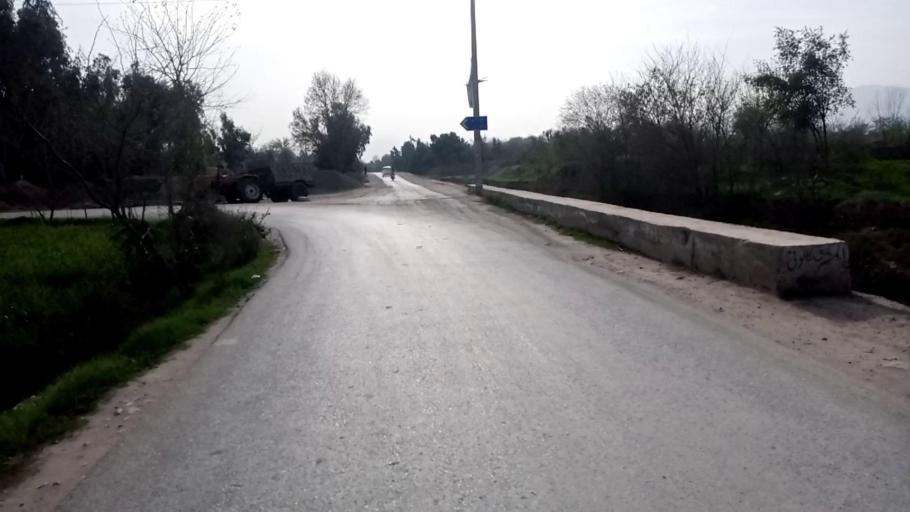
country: PK
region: Khyber Pakhtunkhwa
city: Peshawar
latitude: 34.0216
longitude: 71.4448
